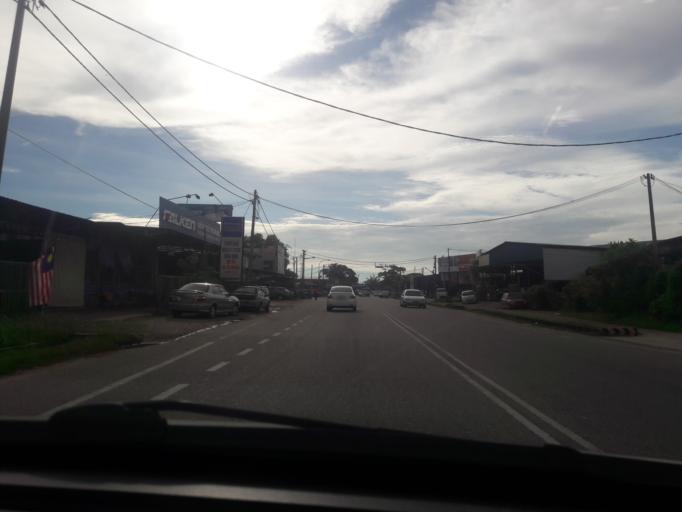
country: MY
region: Kedah
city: Sungai Petani
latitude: 5.6345
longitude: 100.5031
